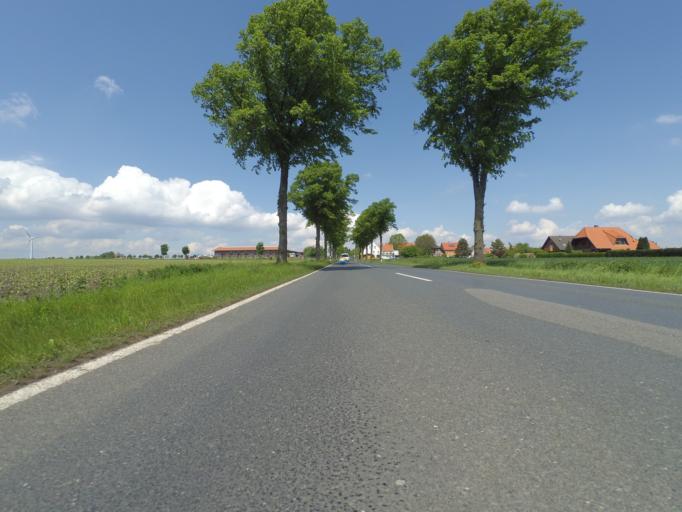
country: DE
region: Lower Saxony
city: Hohenhameln
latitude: 52.2004
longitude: 10.0346
